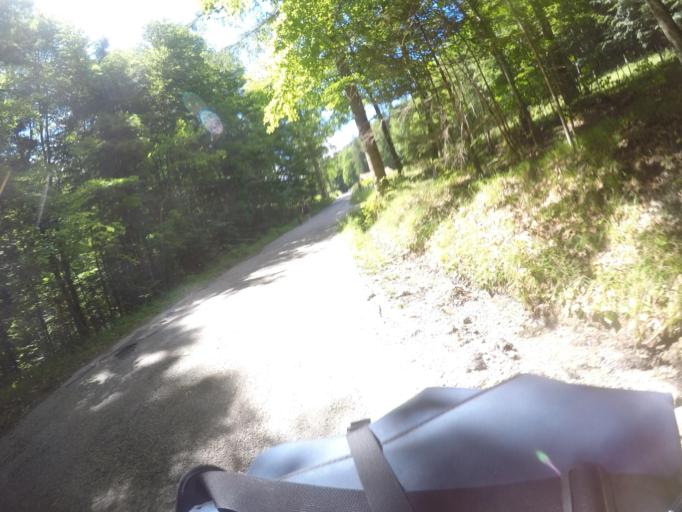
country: AT
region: Tyrol
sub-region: Politischer Bezirk Reutte
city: Vils
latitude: 47.5616
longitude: 10.6530
